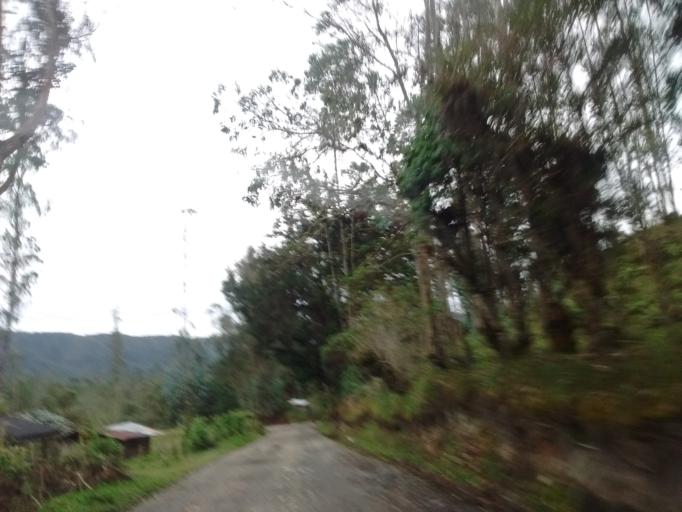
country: CO
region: Huila
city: La Argentina
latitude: 2.2595
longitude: -76.1971
